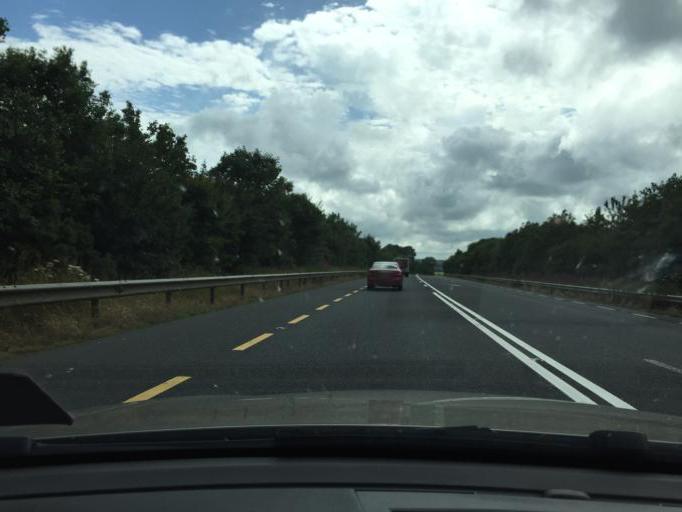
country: IE
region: Munster
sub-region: Waterford
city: Portlaw
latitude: 52.2083
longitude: -7.3985
